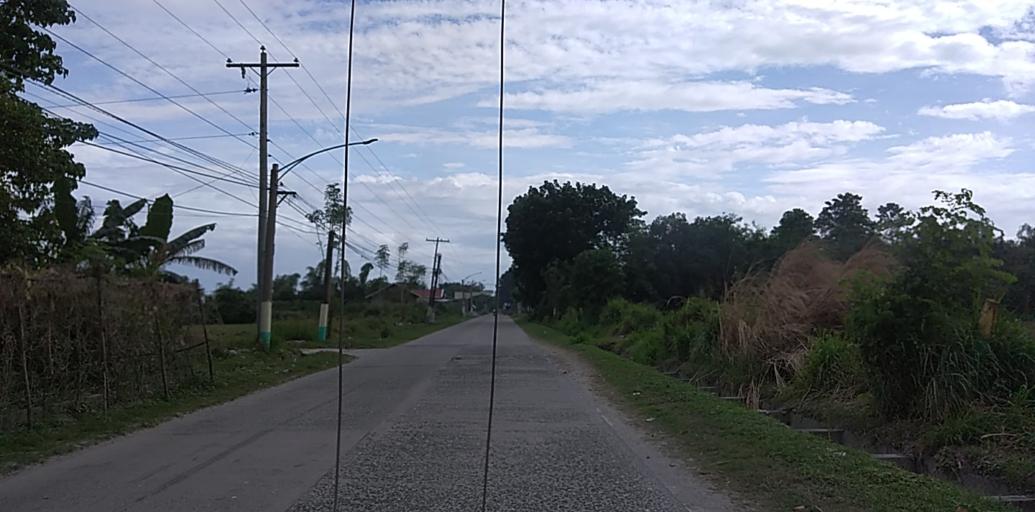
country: PH
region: Central Luzon
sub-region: Province of Pampanga
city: Pulung Santol
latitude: 15.0354
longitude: 120.5655
